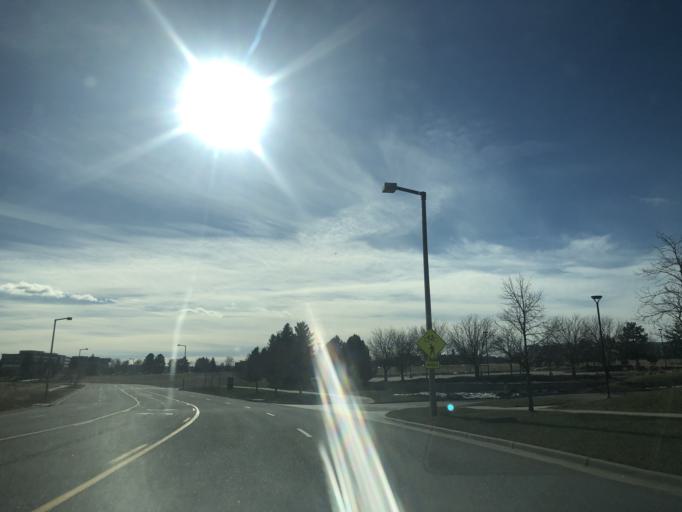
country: US
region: Colorado
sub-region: Douglas County
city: Meridian
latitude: 39.5485
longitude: -104.8659
